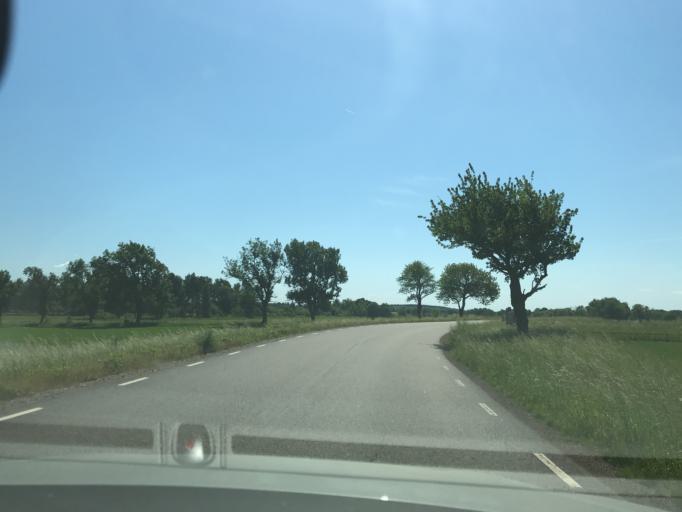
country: SE
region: Vaestra Goetaland
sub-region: Gotene Kommun
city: Kallby
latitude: 58.5714
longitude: 13.3678
